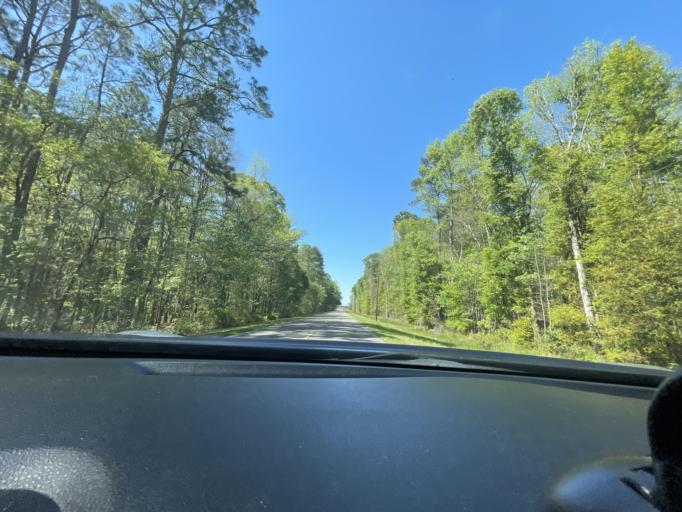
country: US
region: Georgia
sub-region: Chatham County
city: Bloomingdale
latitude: 32.1111
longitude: -81.3119
